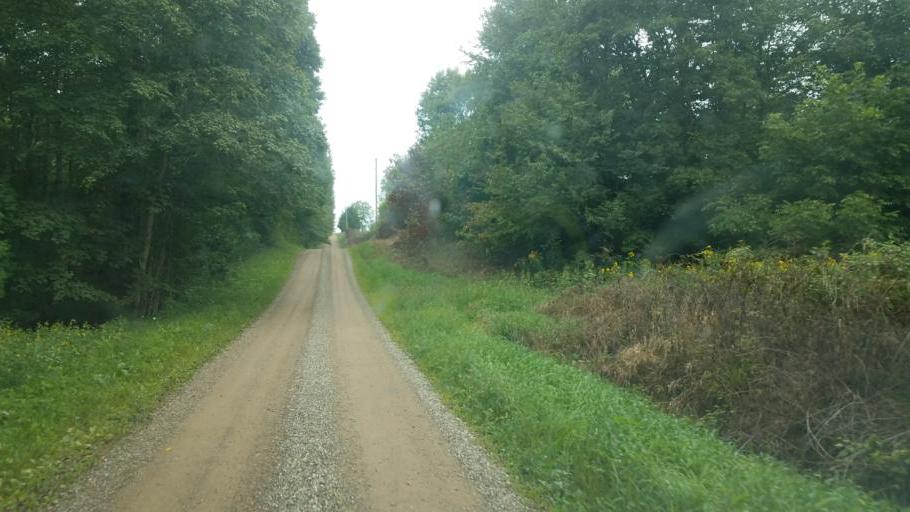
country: US
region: Ohio
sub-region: Licking County
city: Utica
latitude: 40.2707
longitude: -82.4060
